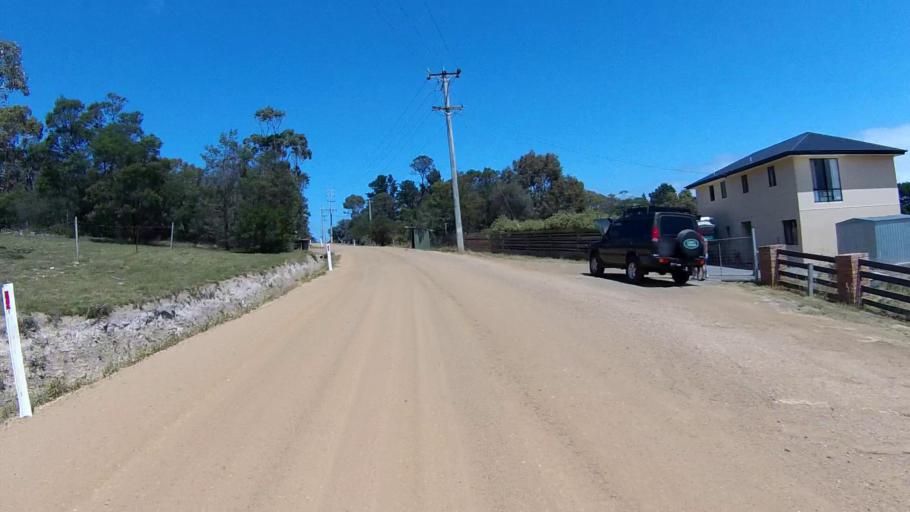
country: AU
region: Tasmania
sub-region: Clarence
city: Lauderdale
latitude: -42.9372
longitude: 147.4607
